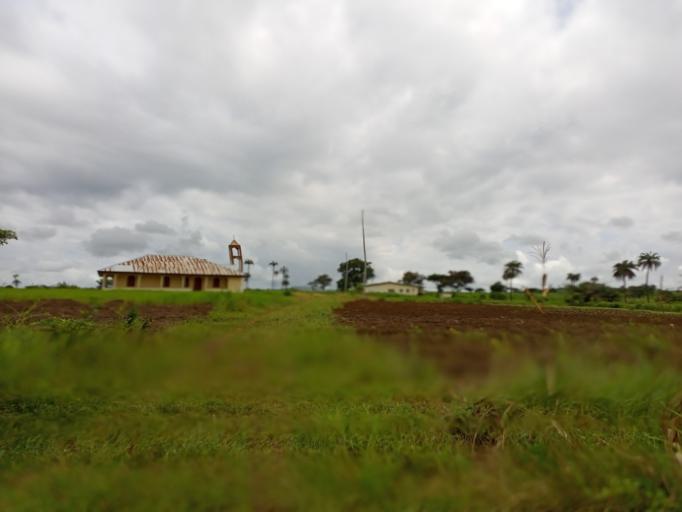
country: SL
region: Northern Province
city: Kamakwie
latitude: 9.5036
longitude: -12.2568
